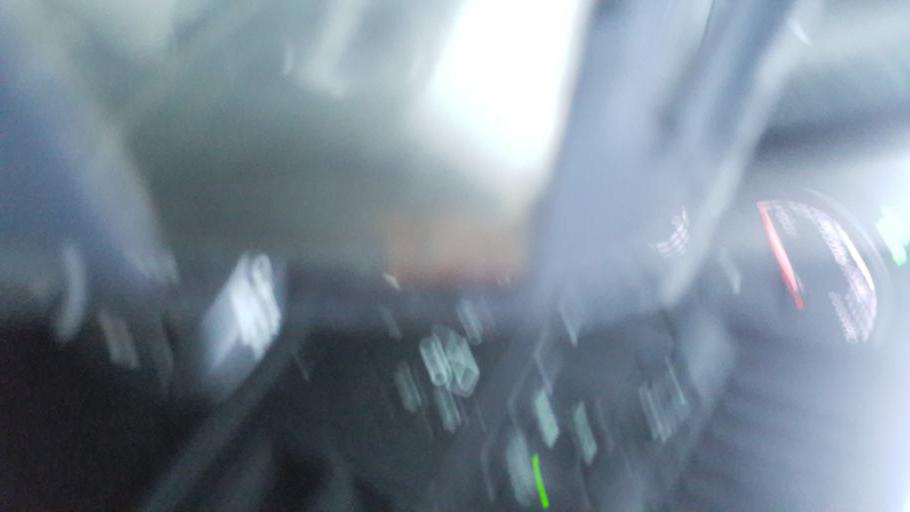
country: IT
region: Lombardy
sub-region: Provincia di Bergamo
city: Orio al Serio
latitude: 45.6965
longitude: 9.6898
